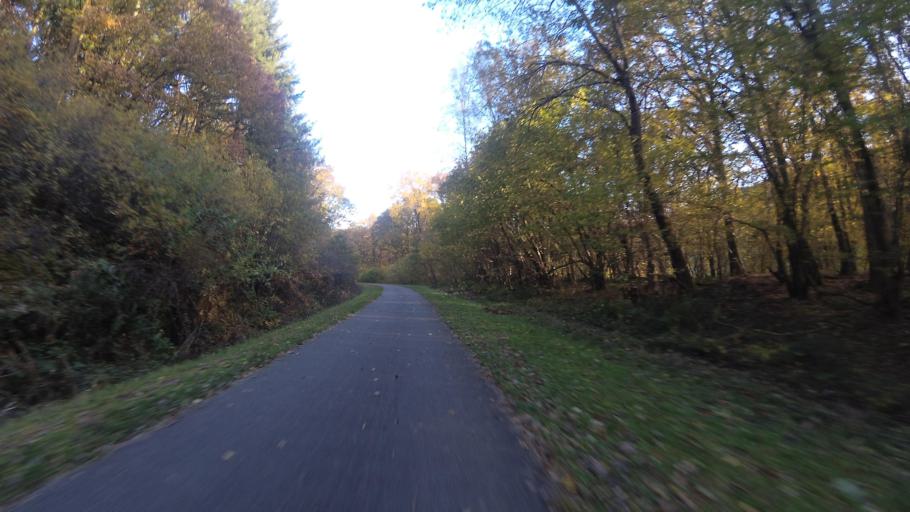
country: DE
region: Rheinland-Pfalz
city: Hentern
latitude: 49.6055
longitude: 6.7128
